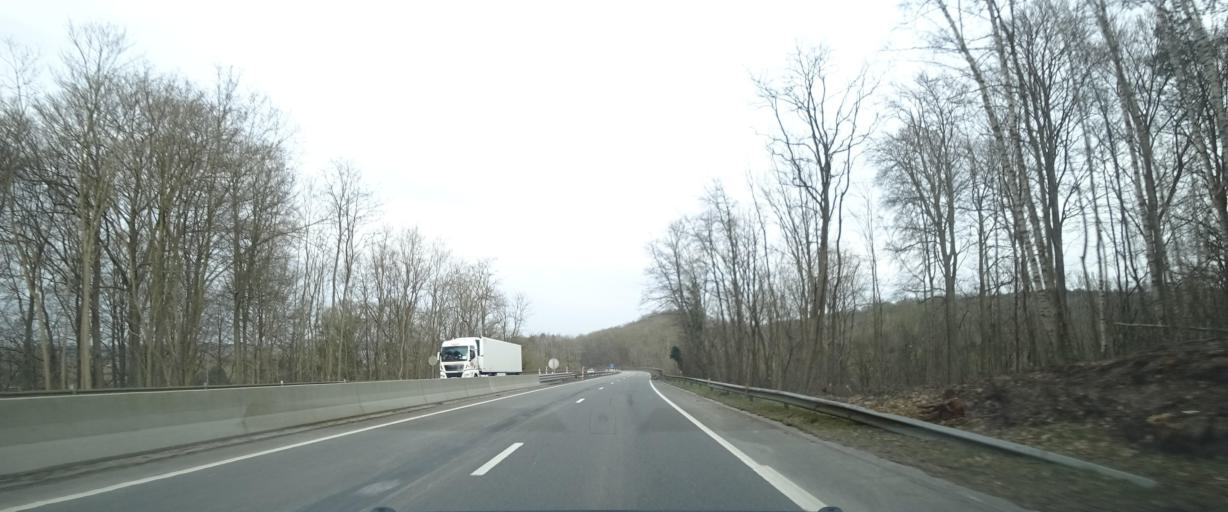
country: BE
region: Wallonia
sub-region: Province du Brabant Wallon
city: Ottignies
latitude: 50.6731
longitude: 4.5833
